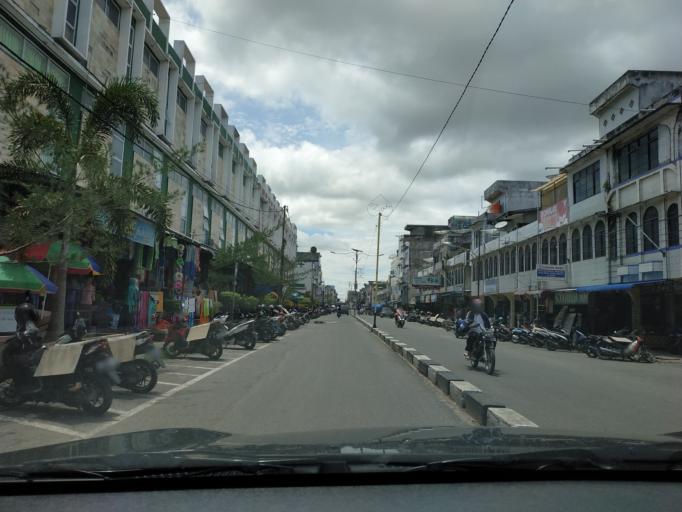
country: ID
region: Riau
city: Tembilahan
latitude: -0.3277
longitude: 103.1582
